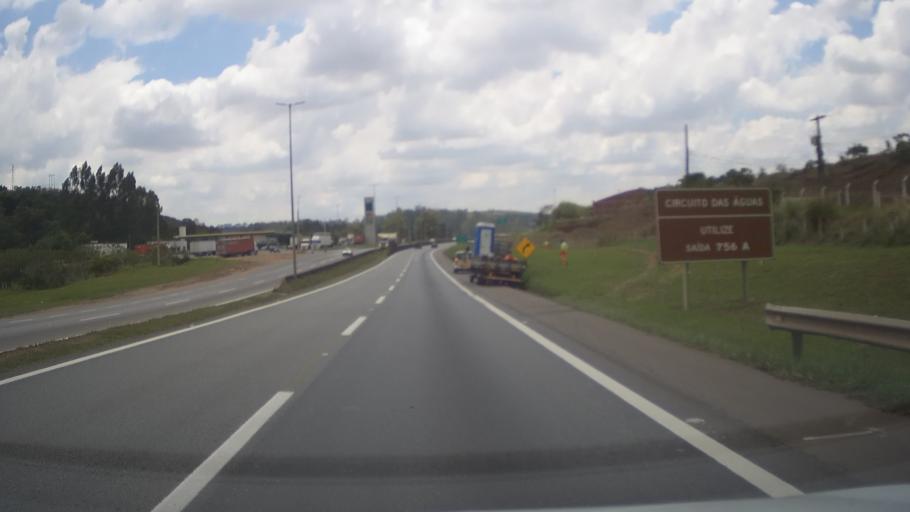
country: BR
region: Minas Gerais
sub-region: Tres Coracoes
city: Tres Coracoes
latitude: -21.6775
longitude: -45.3403
